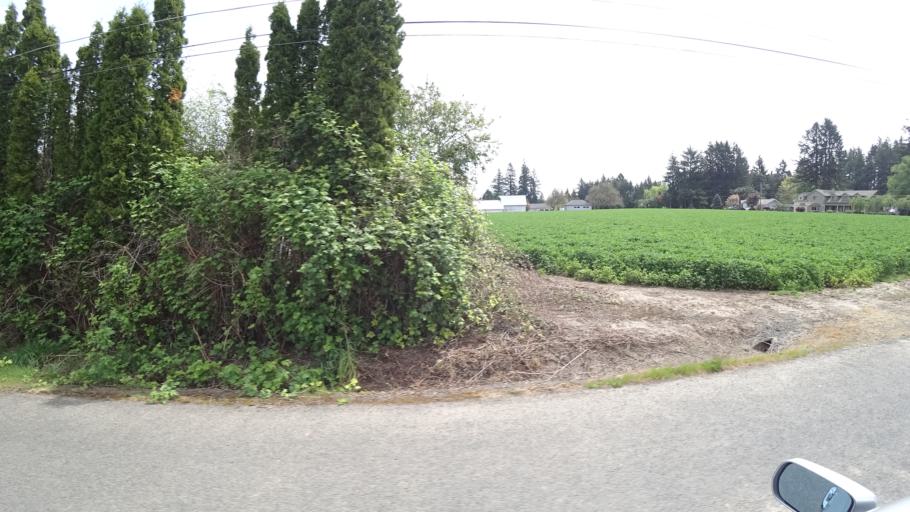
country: US
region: Oregon
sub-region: Washington County
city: Hillsboro
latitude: 45.5337
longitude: -123.0108
